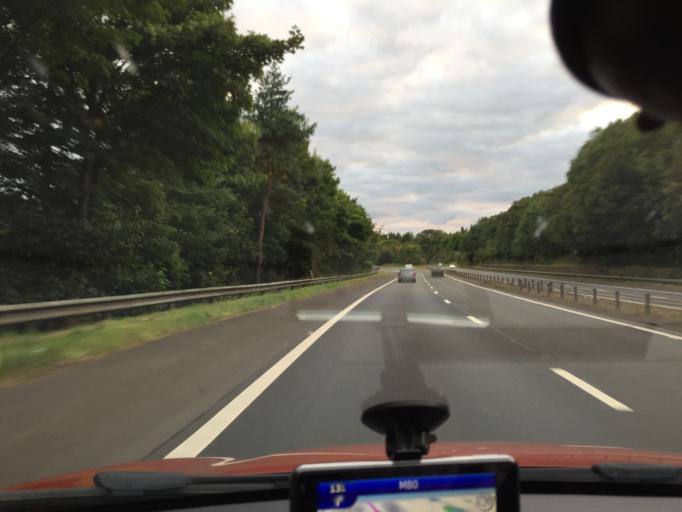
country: GB
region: Scotland
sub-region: Falkirk
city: Bonnybridge
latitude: 56.0021
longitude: -3.9096
